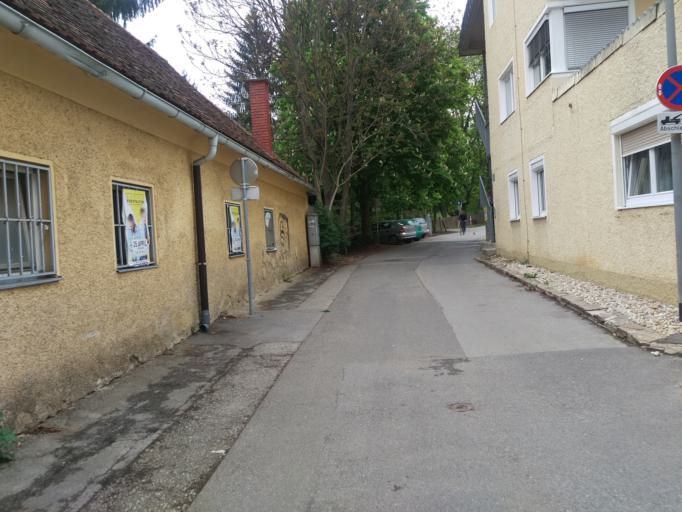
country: AT
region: Styria
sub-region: Graz Stadt
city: Graz
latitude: 47.0808
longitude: 15.4509
